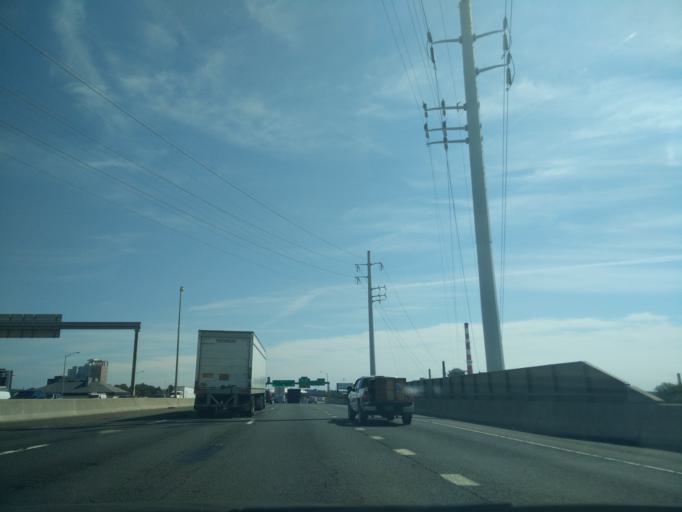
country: US
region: Connecticut
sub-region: Fairfield County
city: Bridgeport
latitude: 41.1690
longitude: -73.1977
